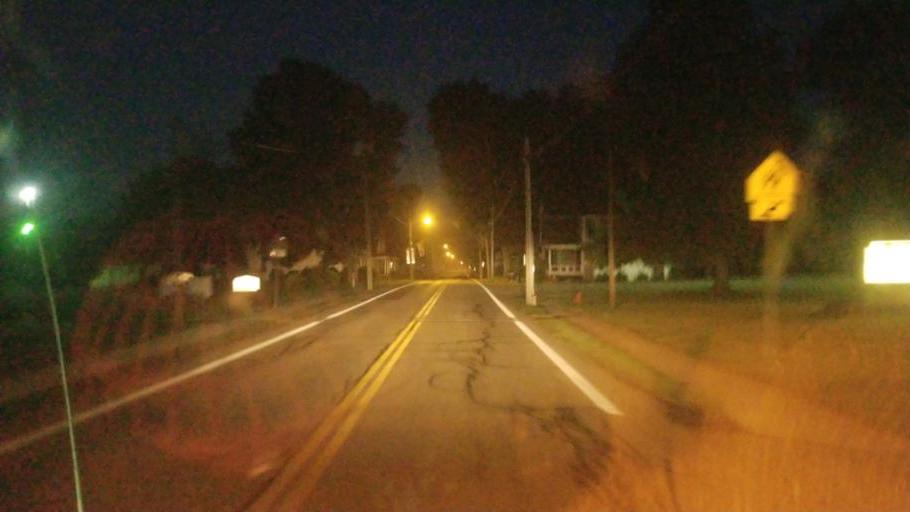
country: US
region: Ohio
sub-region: Perry County
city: Somerset
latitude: 39.8874
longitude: -82.3148
